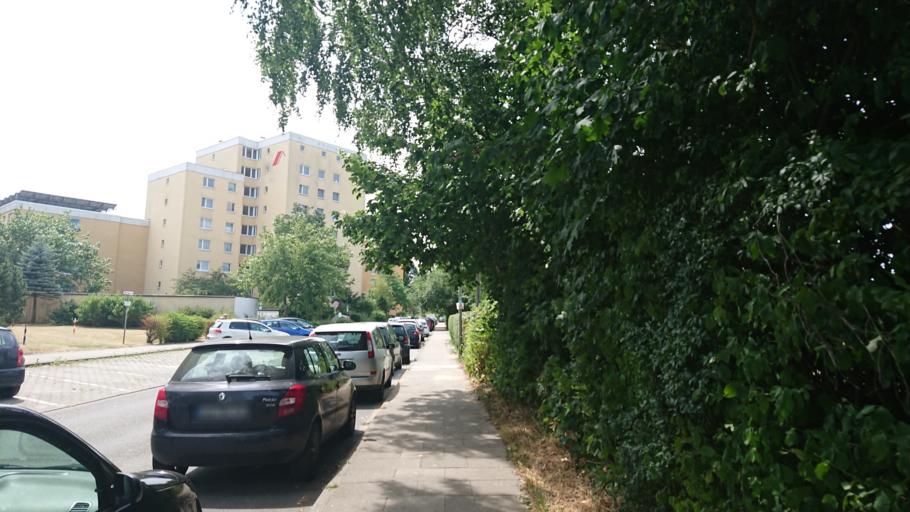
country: DE
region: Hamburg
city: Harburg
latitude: 53.4522
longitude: 9.9693
